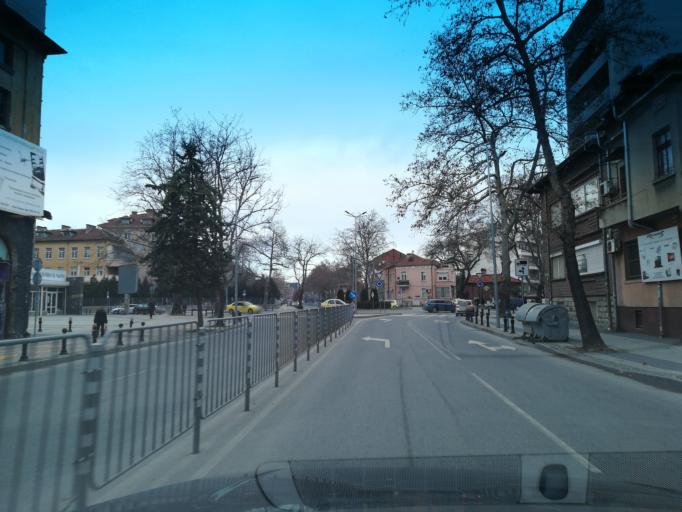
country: BG
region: Plovdiv
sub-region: Obshtina Plovdiv
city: Plovdiv
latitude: 42.1384
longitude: 24.7392
